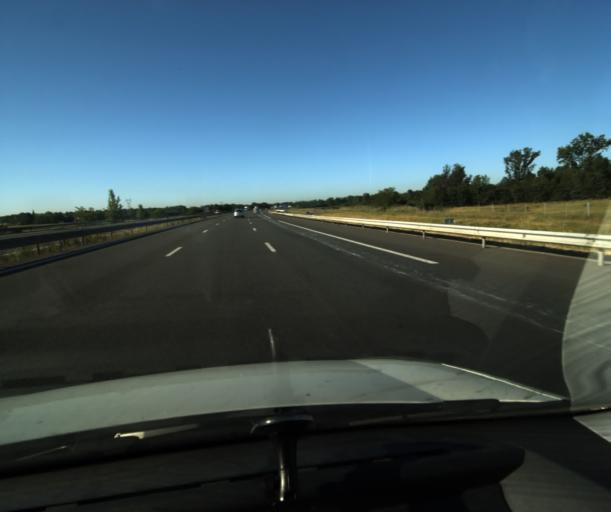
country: FR
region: Midi-Pyrenees
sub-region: Departement du Tarn-et-Garonne
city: Campsas
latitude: 43.9113
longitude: 1.3191
